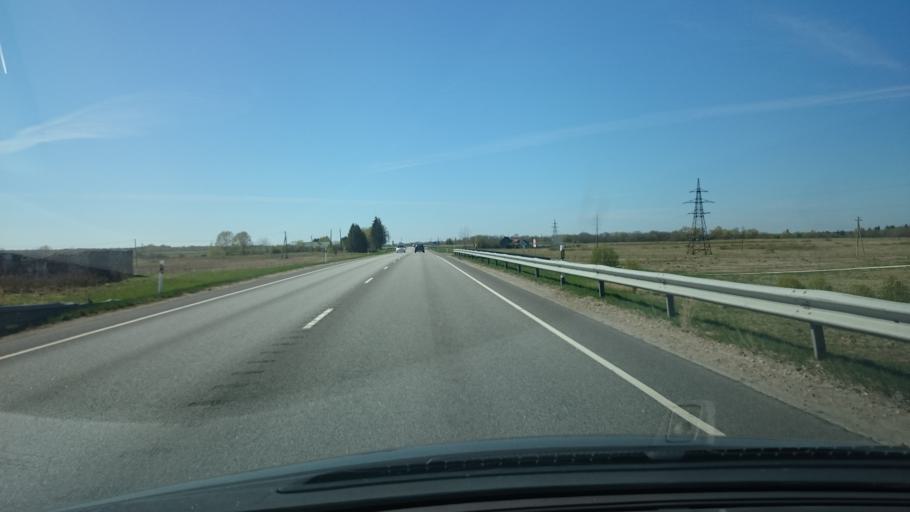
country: EE
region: Ida-Virumaa
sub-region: Narva-Joesuu linn
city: Narva-Joesuu
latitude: 59.4061
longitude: 28.0395
